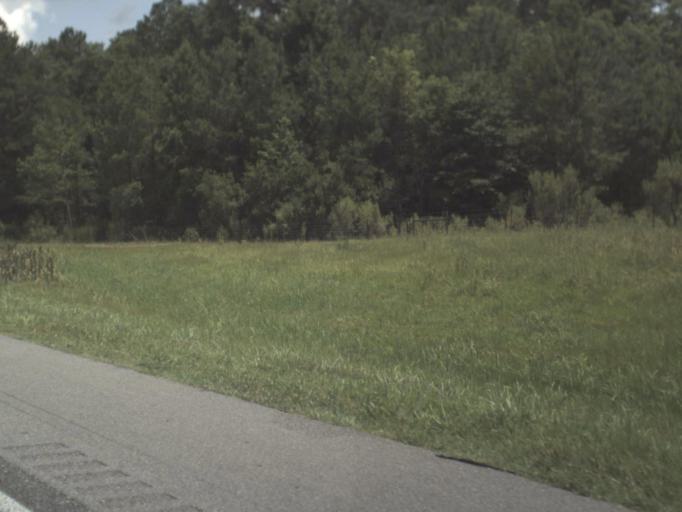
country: US
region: Florida
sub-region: Suwannee County
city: Wellborn
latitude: 30.3656
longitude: -82.8543
